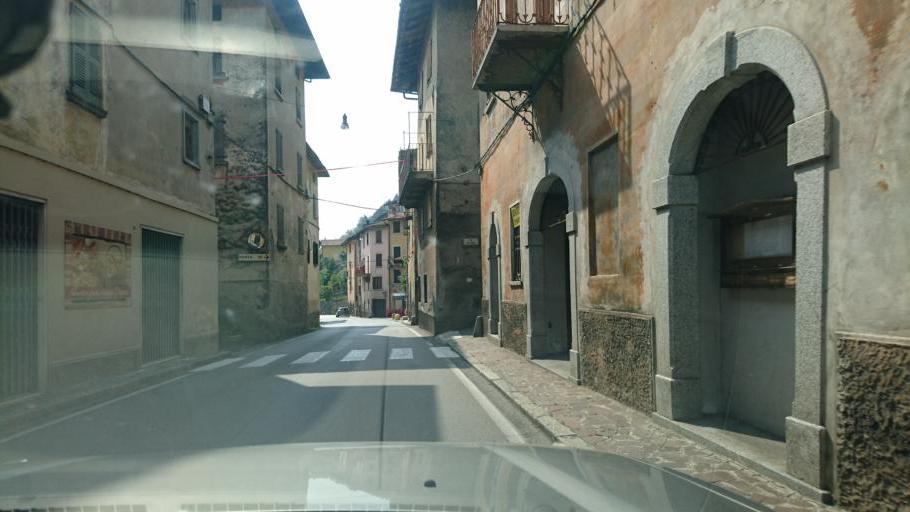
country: IT
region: Lombardy
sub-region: Provincia di Brescia
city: Anfo
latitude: 45.7668
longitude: 10.4923
